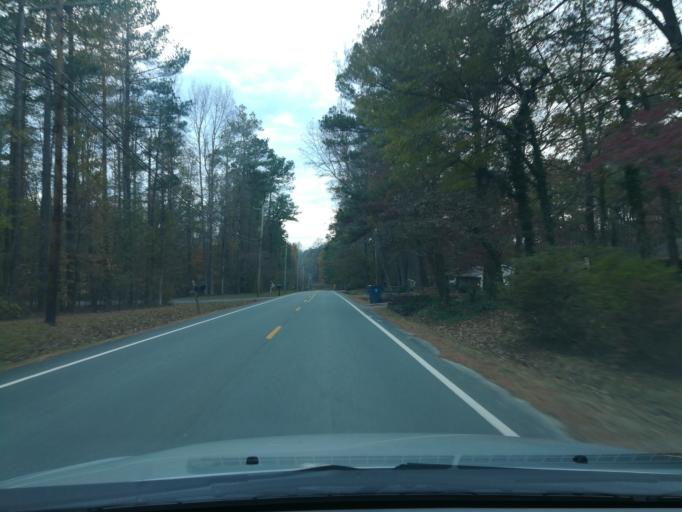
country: US
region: North Carolina
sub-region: Orange County
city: Hillsborough
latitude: 36.0302
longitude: -79.0053
